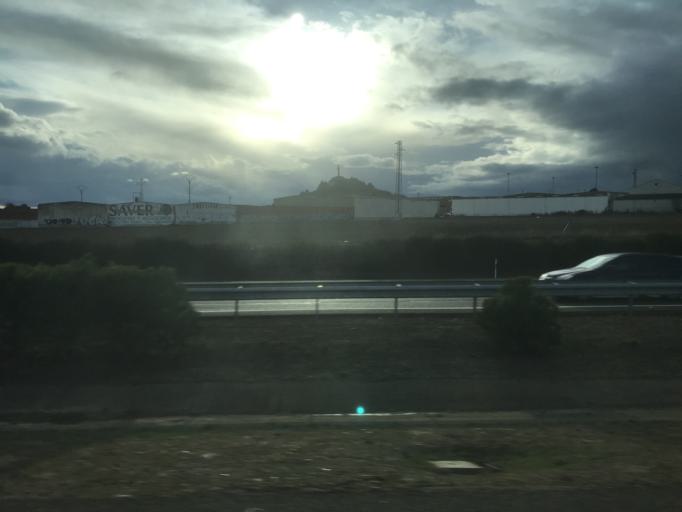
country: ES
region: Castille and Leon
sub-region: Provincia de Palencia
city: Villalobon
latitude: 42.0314
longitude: -4.5172
